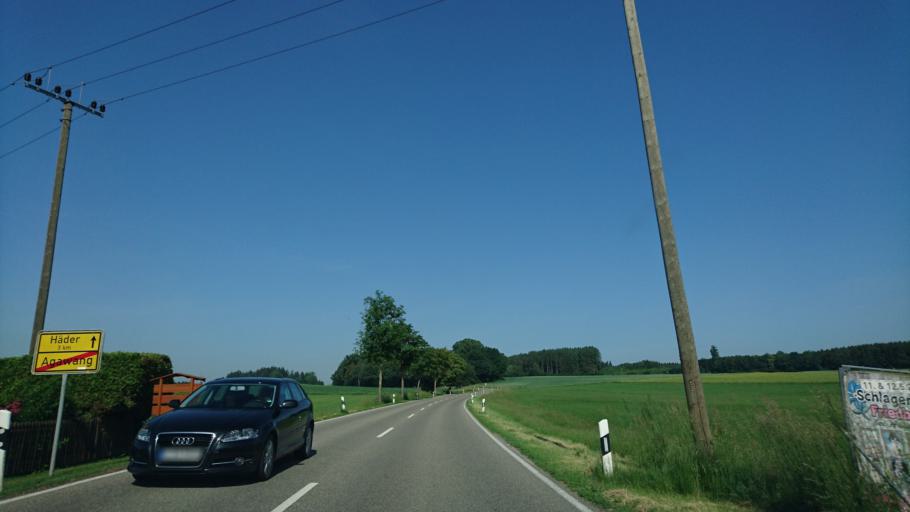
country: DE
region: Bavaria
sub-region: Swabia
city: Horgau
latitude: 48.3618
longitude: 10.6802
